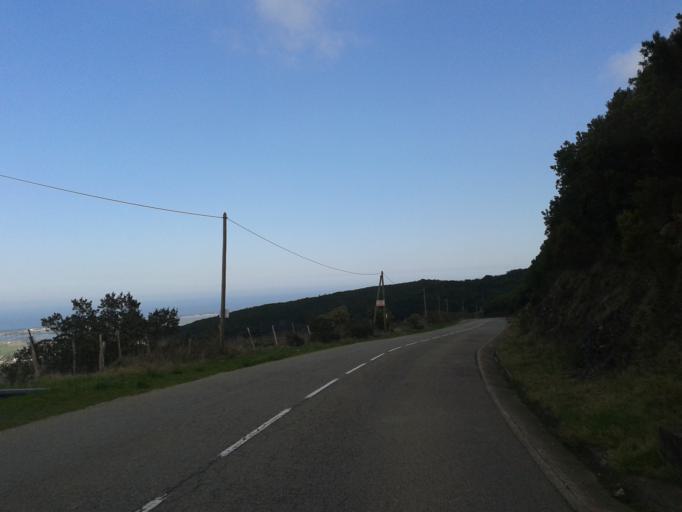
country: FR
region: Corsica
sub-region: Departement de la Haute-Corse
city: Biguglia
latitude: 42.5992
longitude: 9.4038
